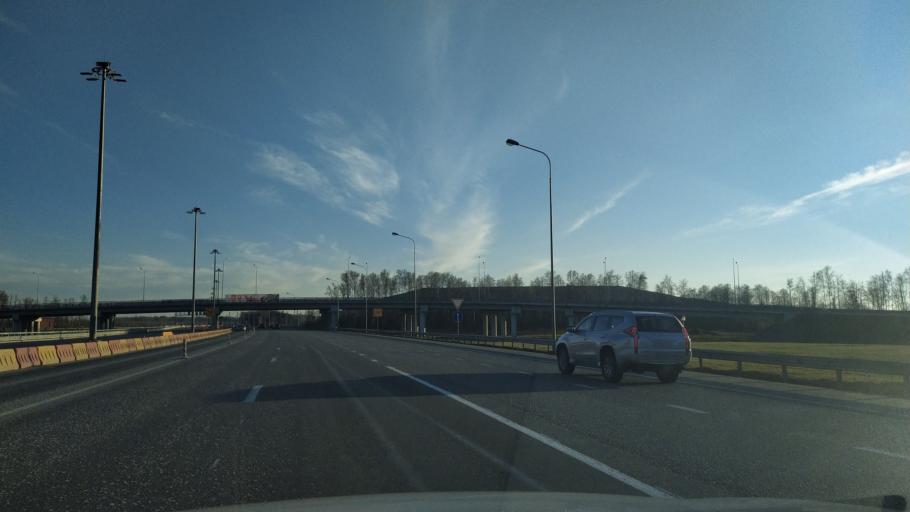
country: RU
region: St.-Petersburg
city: Levashovo
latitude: 60.0765
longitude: 30.1825
